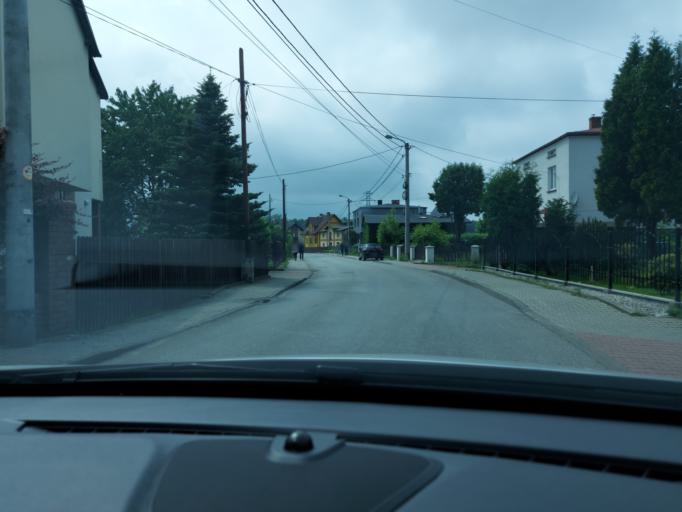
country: PL
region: Silesian Voivodeship
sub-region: Tychy
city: Tychy
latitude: 50.1097
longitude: 18.9606
